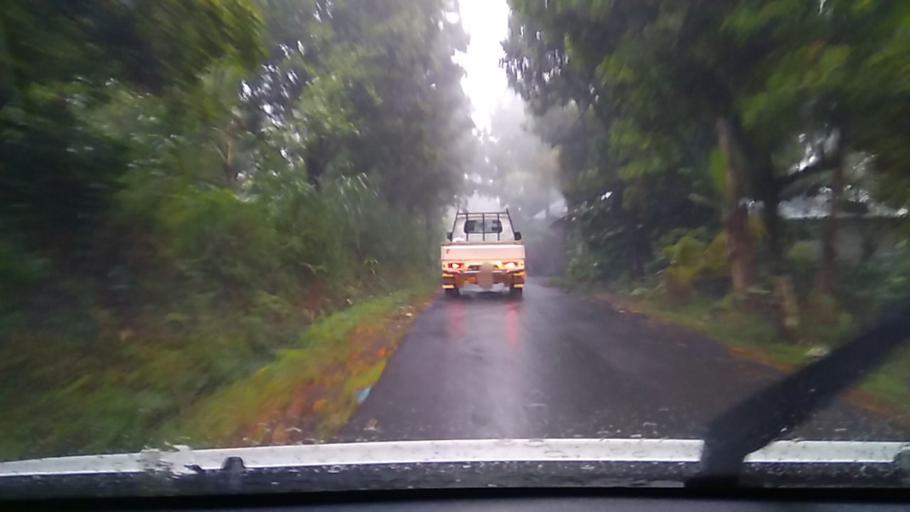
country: ID
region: Bali
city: Banjar Ambengan
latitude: -8.2067
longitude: 115.1723
